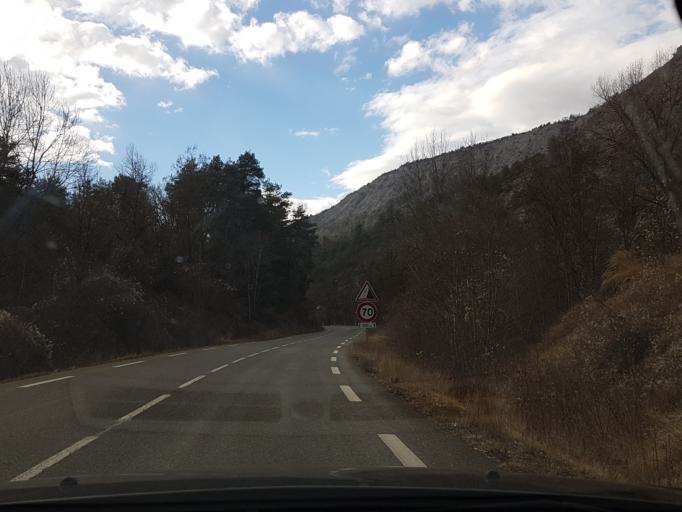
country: FR
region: Provence-Alpes-Cote d'Azur
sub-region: Departement des Hautes-Alpes
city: Tallard
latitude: 44.4936
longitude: 6.0817
